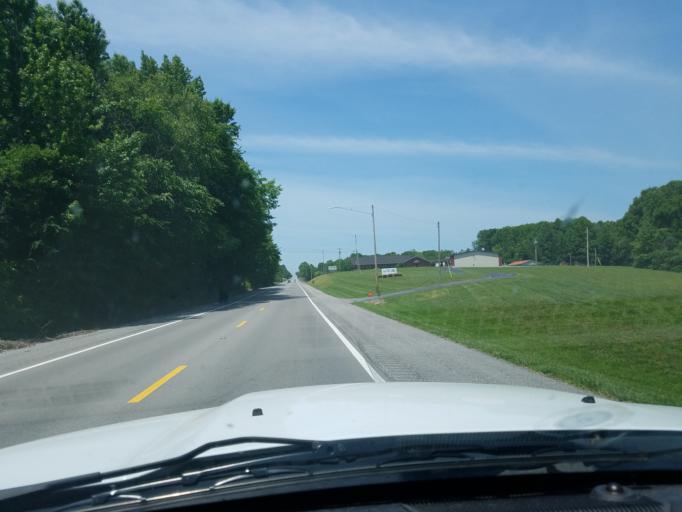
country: US
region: Tennessee
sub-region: Sumner County
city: Westmoreland
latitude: 36.5679
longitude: -86.2398
